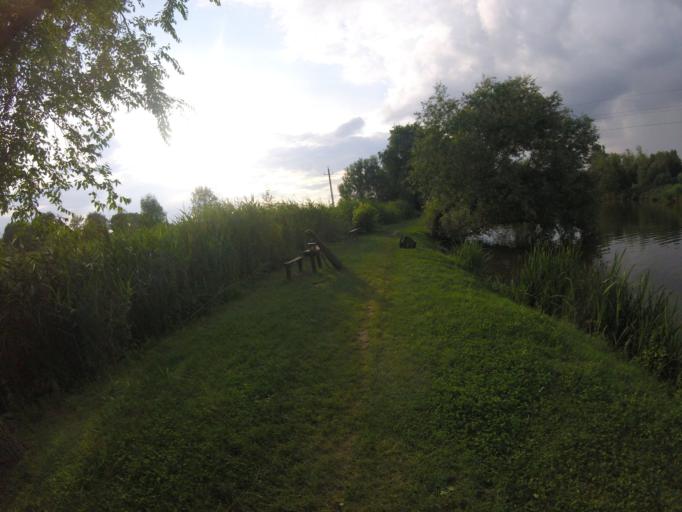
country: HU
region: Pest
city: Albertirsa
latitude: 47.2562
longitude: 19.6012
